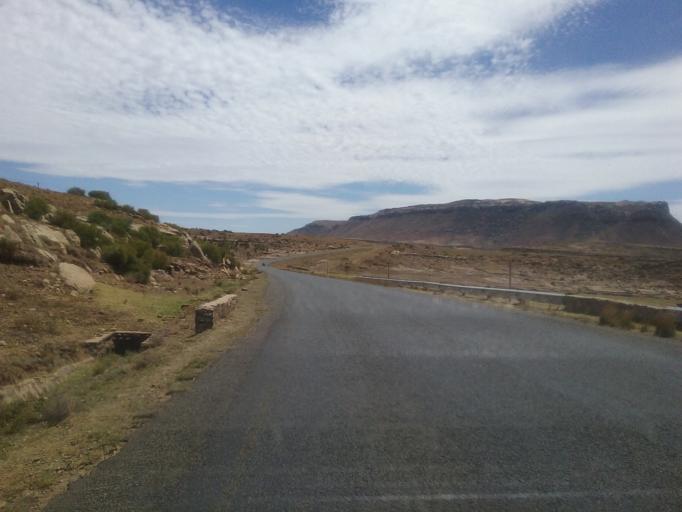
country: LS
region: Mafeteng
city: Mafeteng
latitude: -29.9056
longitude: 27.2515
